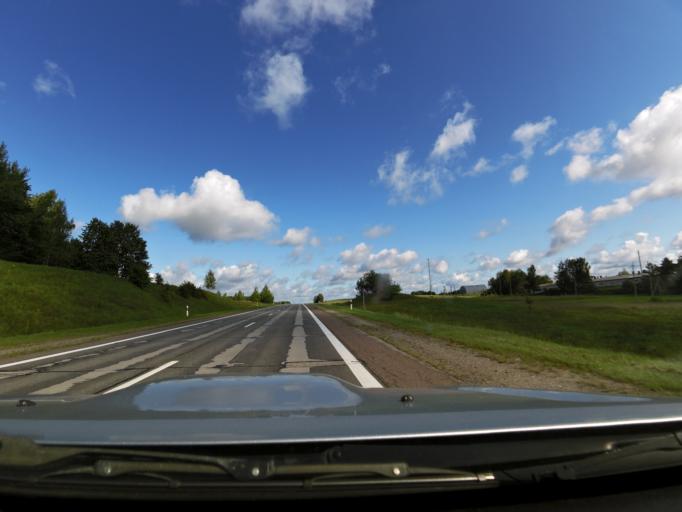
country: LT
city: Moletai
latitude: 55.3465
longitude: 25.5144
